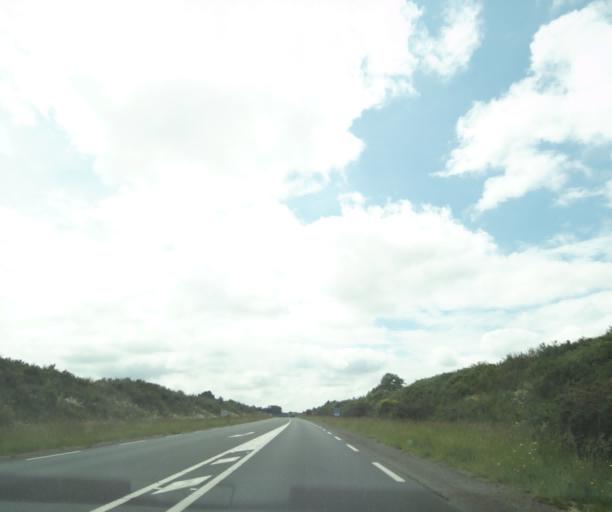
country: FR
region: Poitou-Charentes
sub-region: Departement des Deux-Sevres
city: Saint-Pardoux
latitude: 46.5388
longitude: -0.3144
